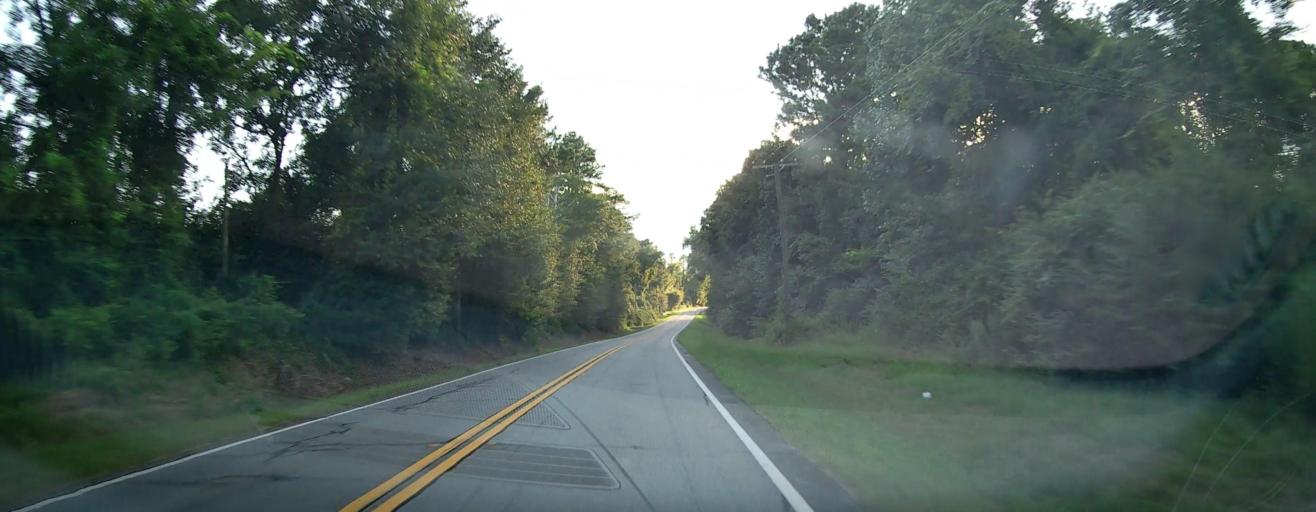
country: US
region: Georgia
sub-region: Pulaski County
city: Hawkinsville
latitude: 32.2659
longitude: -83.5173
